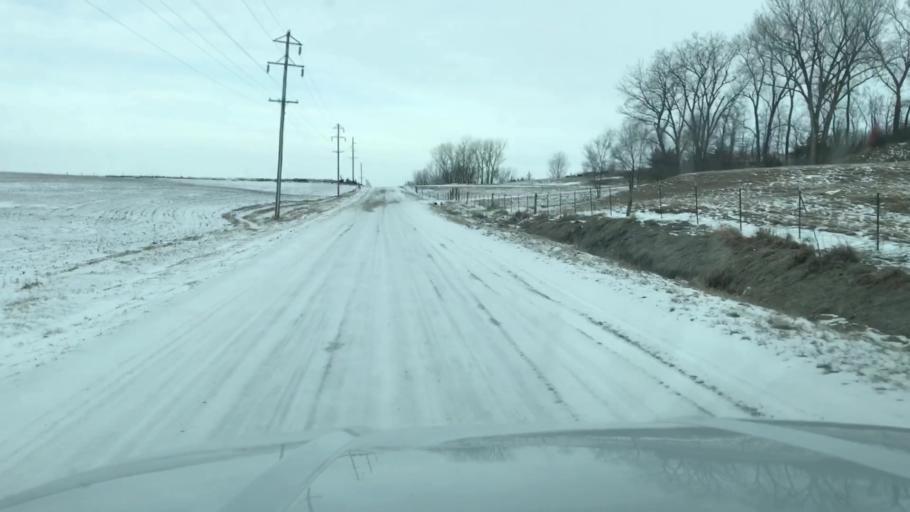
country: US
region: Missouri
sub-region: Holt County
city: Oregon
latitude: 40.1301
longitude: -95.0579
